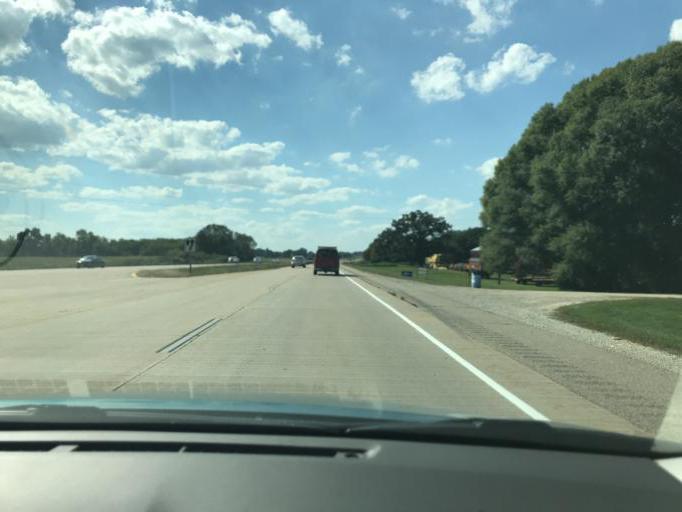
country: US
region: Wisconsin
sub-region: Kenosha County
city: Twin Lakes
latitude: 42.5821
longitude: -88.2283
